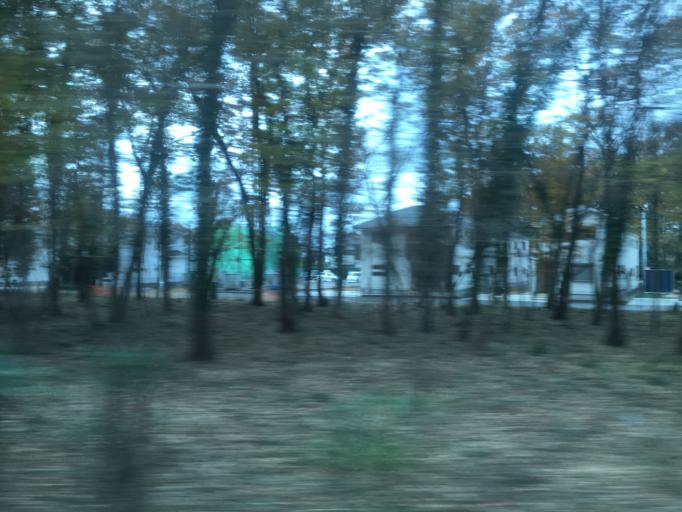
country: JP
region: Saitama
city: Okegawa
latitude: 36.0212
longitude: 139.5420
